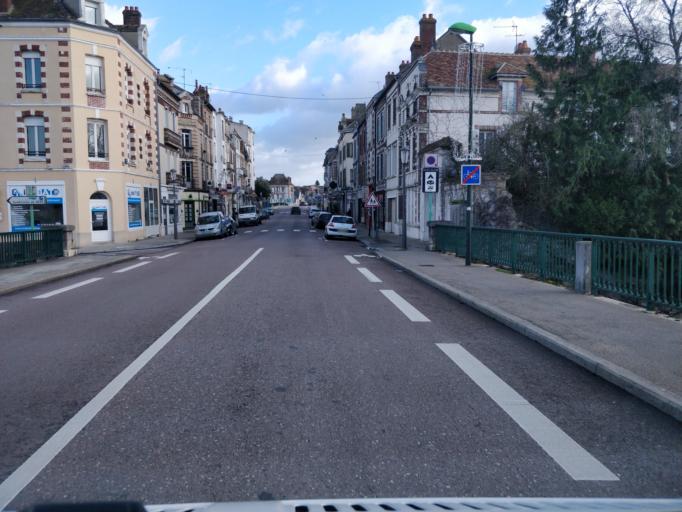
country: FR
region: Bourgogne
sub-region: Departement de l'Yonne
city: Sens
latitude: 48.1977
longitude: 3.2737
